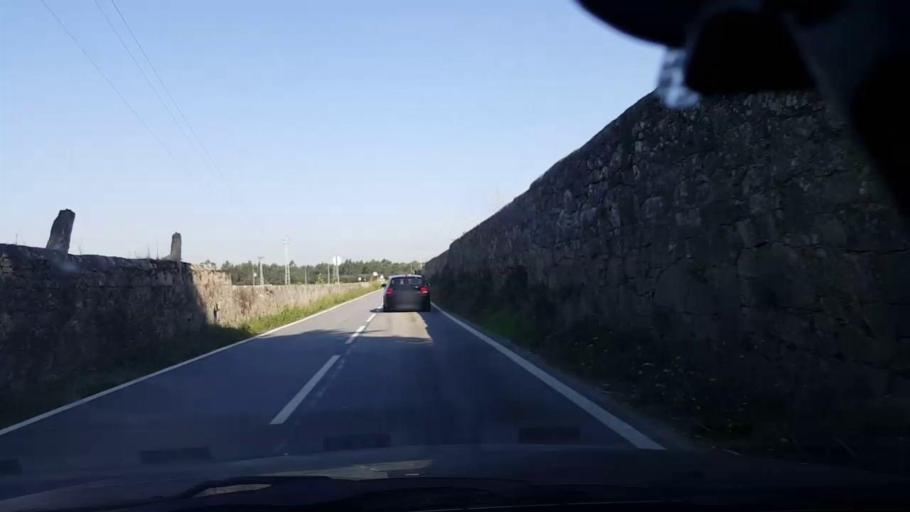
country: PT
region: Porto
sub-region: Vila do Conde
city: Arvore
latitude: 41.3240
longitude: -8.6809
